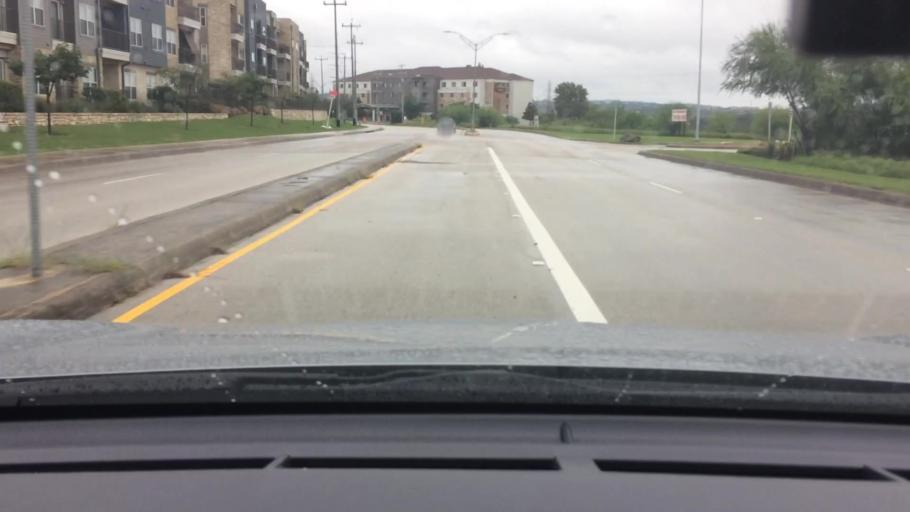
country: US
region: Texas
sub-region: Bexar County
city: Hollywood Park
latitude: 29.6121
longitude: -98.4626
